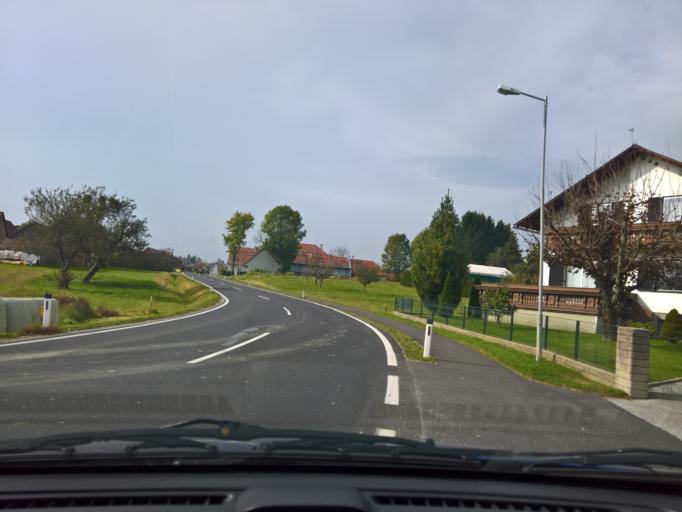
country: AT
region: Styria
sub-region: Politischer Bezirk Deutschlandsberg
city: Gross Sankt Florian
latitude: 46.8276
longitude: 15.3281
